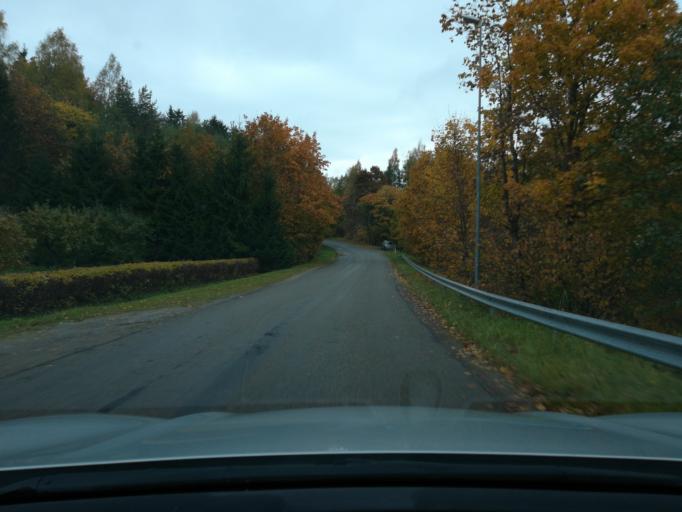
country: EE
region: Ida-Virumaa
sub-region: Johvi vald
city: Johvi
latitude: 59.1985
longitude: 27.5390
